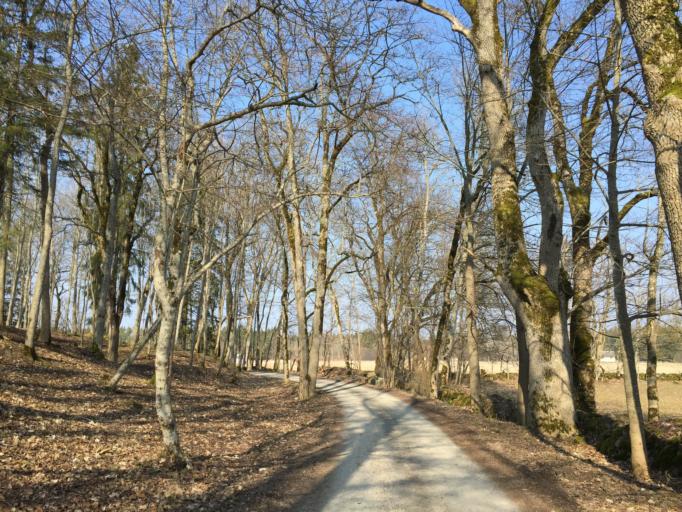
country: EE
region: Saare
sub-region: Kuressaare linn
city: Kuressaare
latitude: 58.3727
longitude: 22.6706
